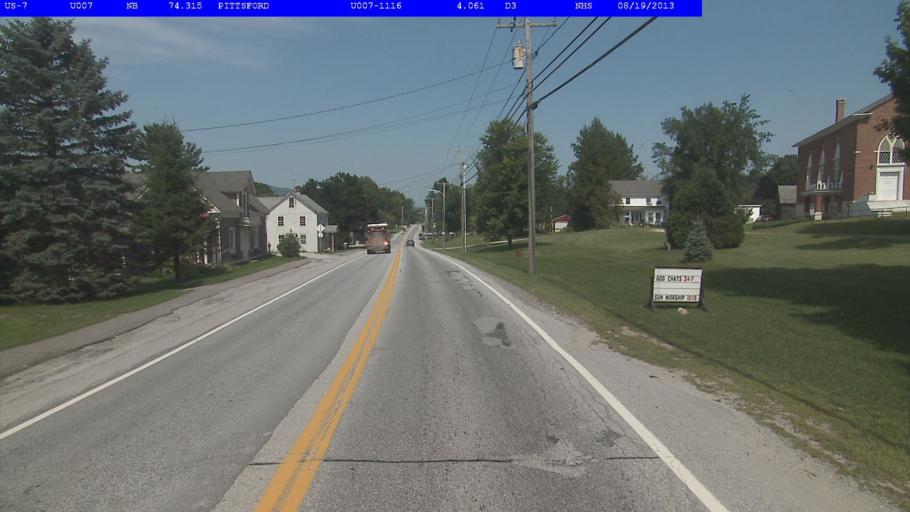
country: US
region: Vermont
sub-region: Rutland County
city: Brandon
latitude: 43.7077
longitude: -73.0289
